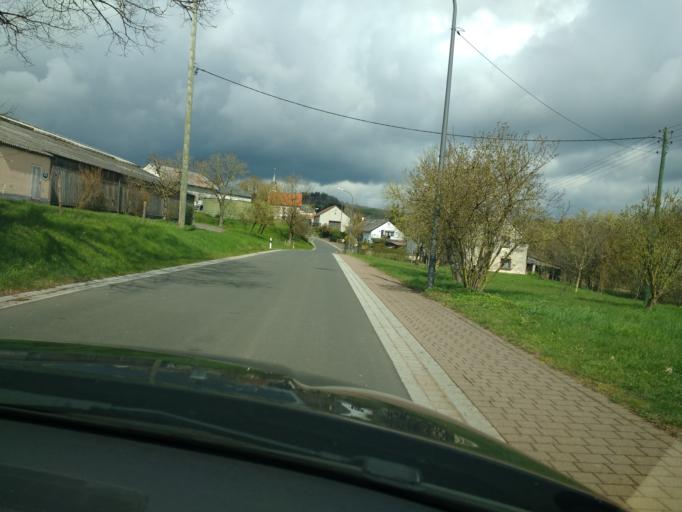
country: DE
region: Rheinland-Pfalz
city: Duppach
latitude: 50.2584
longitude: 6.5697
